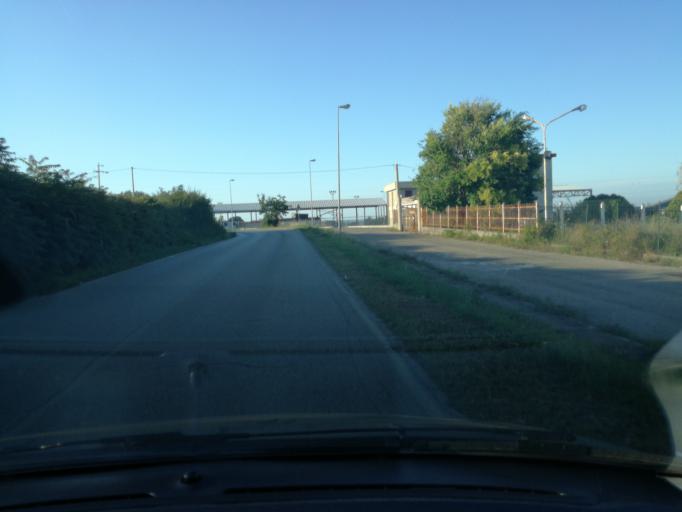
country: IT
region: Molise
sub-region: Provincia di Campobasso
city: San Giacomo degli Schiavoni
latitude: 41.9565
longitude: 14.9445
